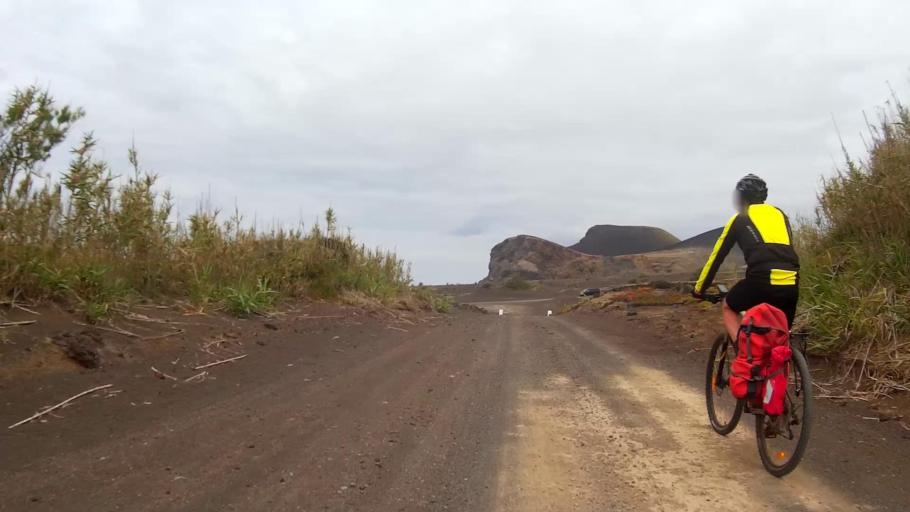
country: PT
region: Azores
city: Ribeira Grande
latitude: 38.5920
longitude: -28.8248
